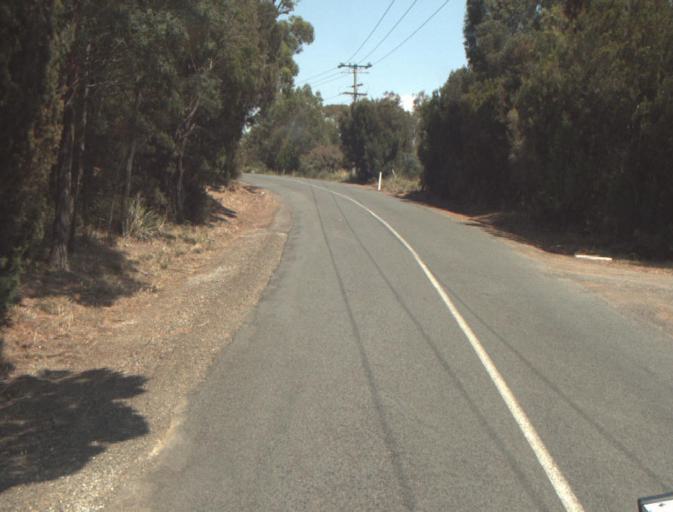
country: AU
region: Tasmania
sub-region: Launceston
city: Newstead
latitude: -41.4971
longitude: 147.2077
